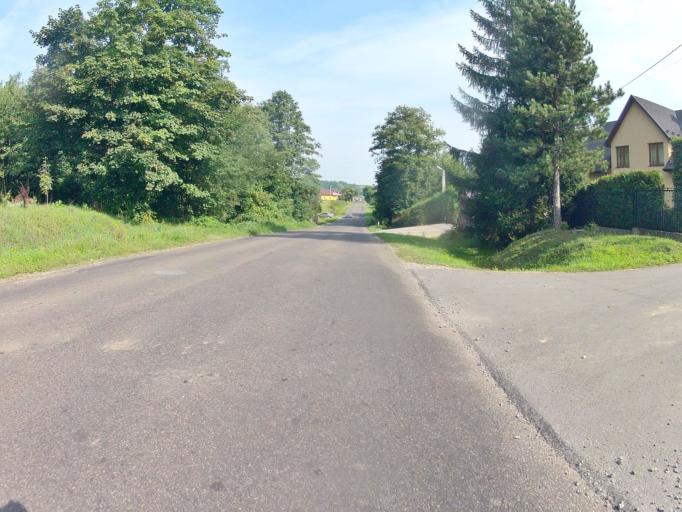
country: PL
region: Subcarpathian Voivodeship
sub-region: Powiat jasielski
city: Brzyska
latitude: 49.7908
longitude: 21.3983
